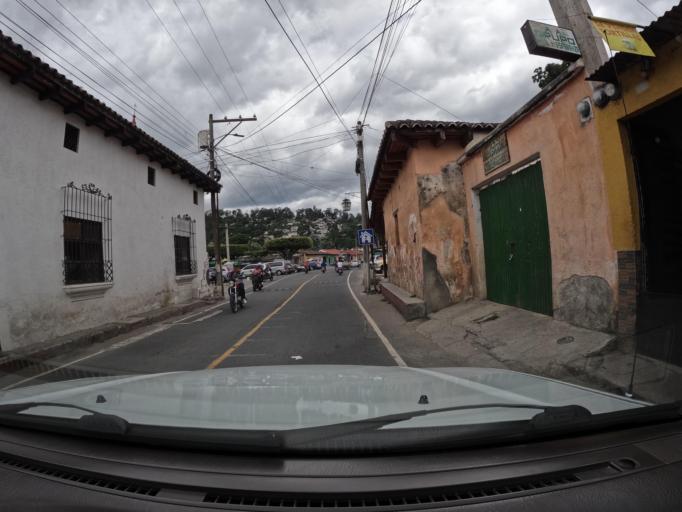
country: GT
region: Sacatepequez
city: Jocotenango
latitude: 14.5734
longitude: -90.7354
